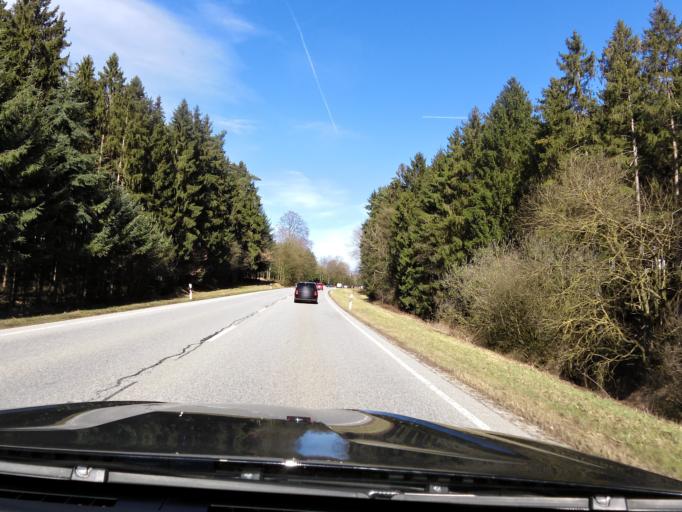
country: DE
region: Bavaria
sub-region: Lower Bavaria
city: Essenbach
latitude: 48.6529
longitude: 12.2114
